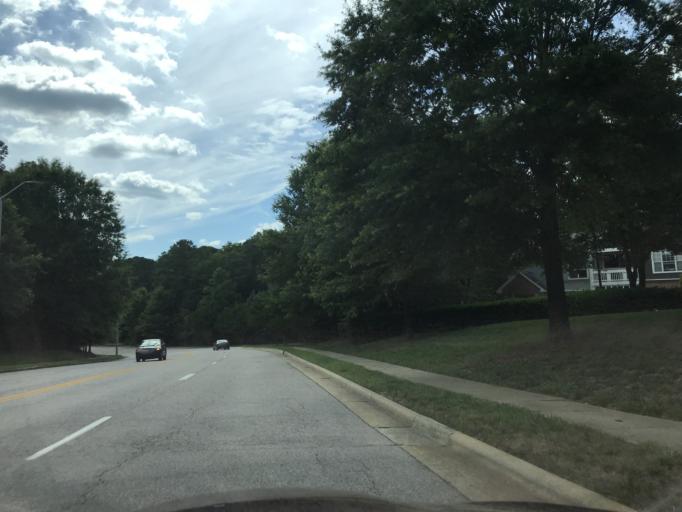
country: US
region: North Carolina
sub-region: Wake County
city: West Raleigh
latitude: 35.9047
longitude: -78.6607
